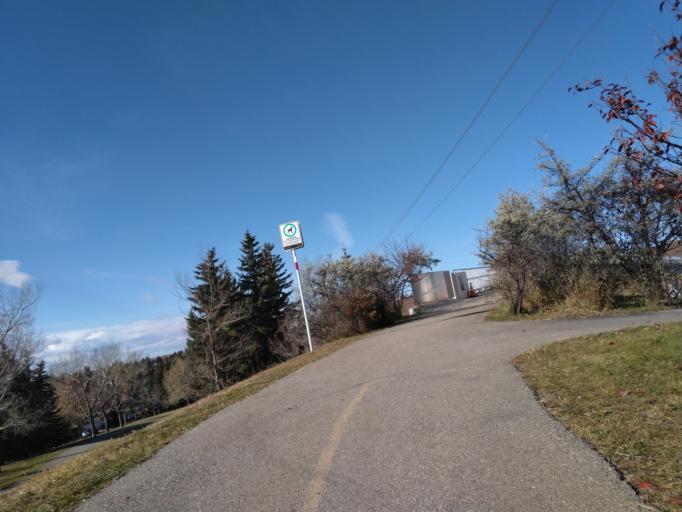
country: CA
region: Alberta
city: Calgary
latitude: 51.1011
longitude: -114.1244
